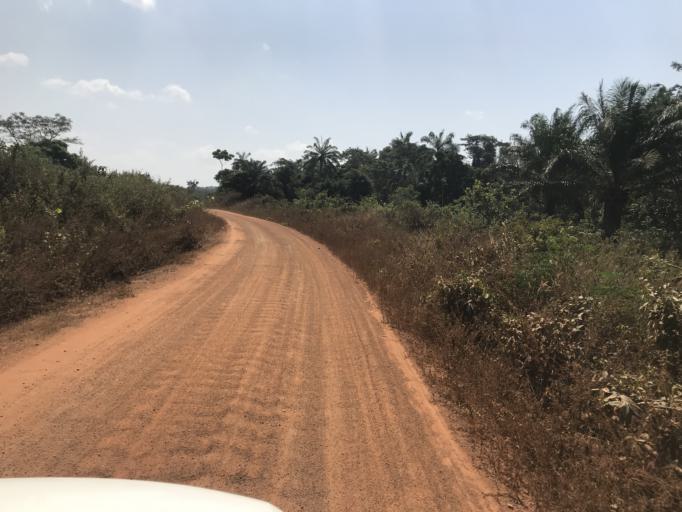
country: NG
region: Osun
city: Ifon
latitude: 7.9101
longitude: 4.4805
